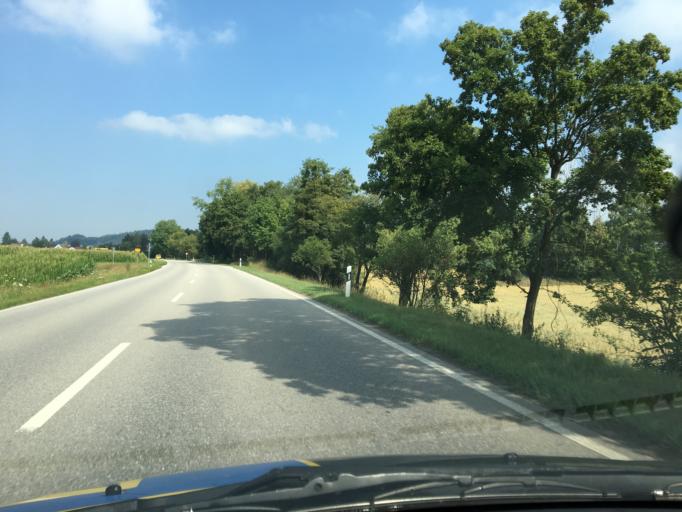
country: DE
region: Bavaria
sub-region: Upper Bavaria
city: Winhoring
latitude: 48.2602
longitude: 12.6612
